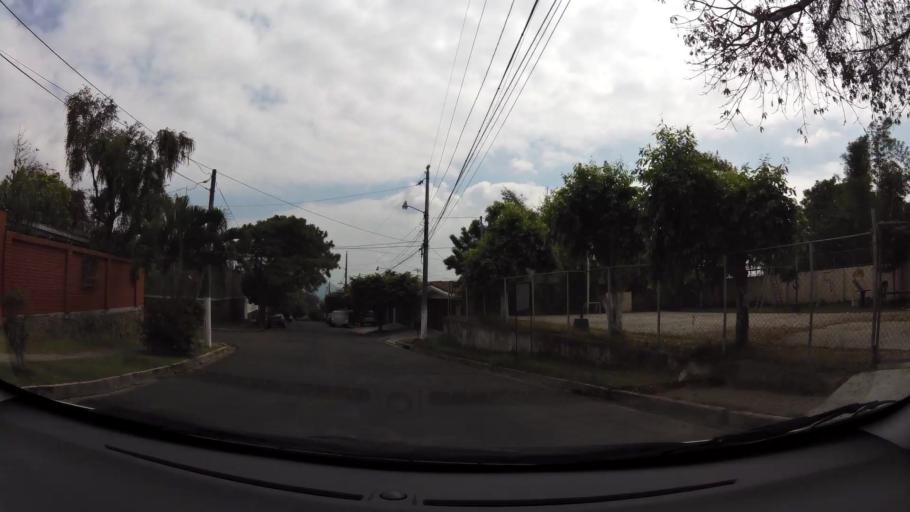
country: SV
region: La Libertad
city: Santa Tecla
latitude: 13.7065
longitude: -89.2538
